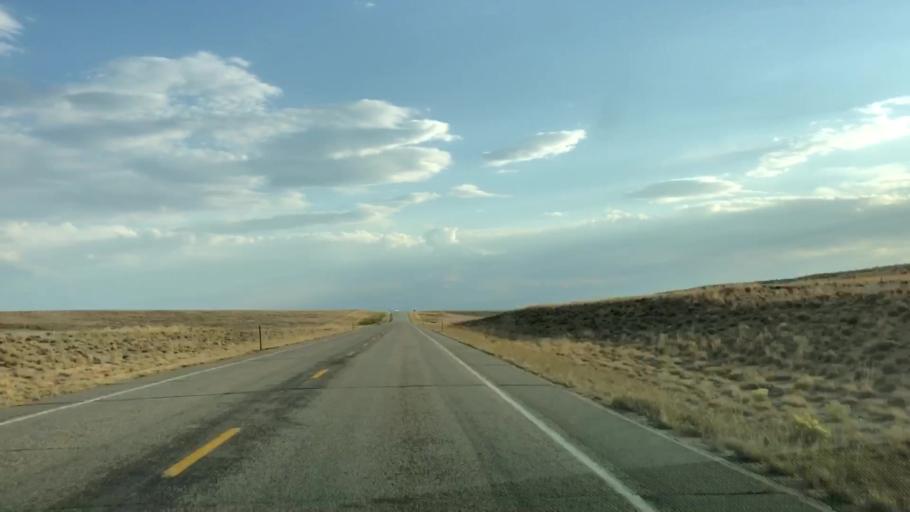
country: US
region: Wyoming
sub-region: Sweetwater County
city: North Rock Springs
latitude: 42.2079
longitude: -109.4743
